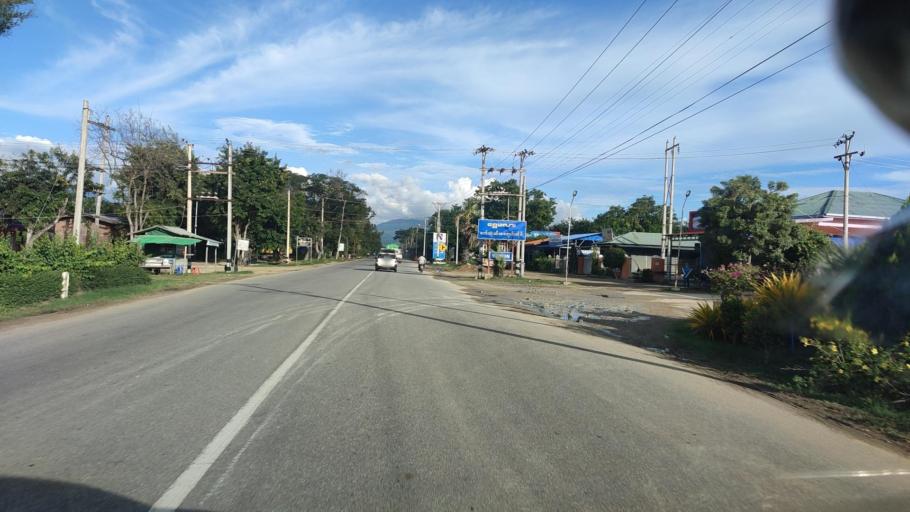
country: MM
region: Mandalay
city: Yamethin
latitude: 20.1174
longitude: 96.2189
